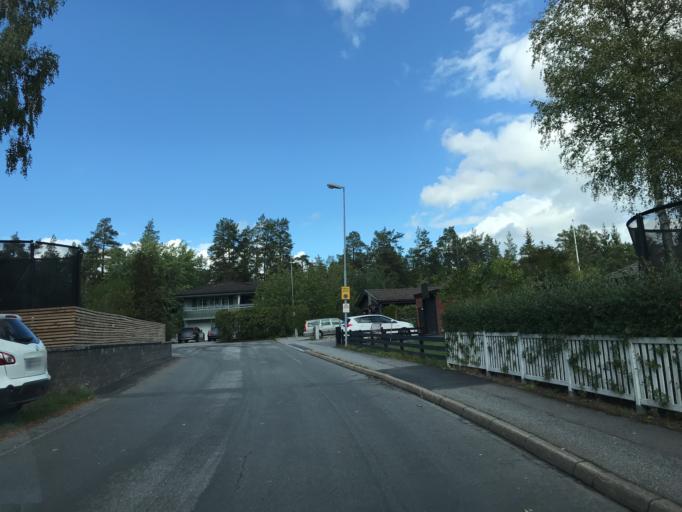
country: SE
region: Stockholm
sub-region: Sollentuna Kommun
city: Sollentuna
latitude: 59.4630
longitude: 17.9458
